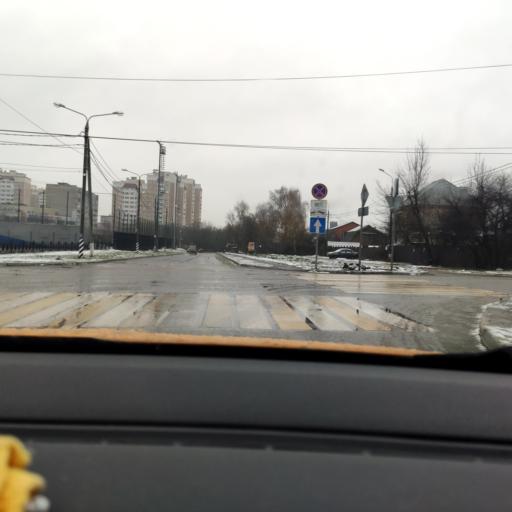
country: RU
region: Moskovskaya
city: Domodedovo
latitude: 55.4492
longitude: 37.7479
